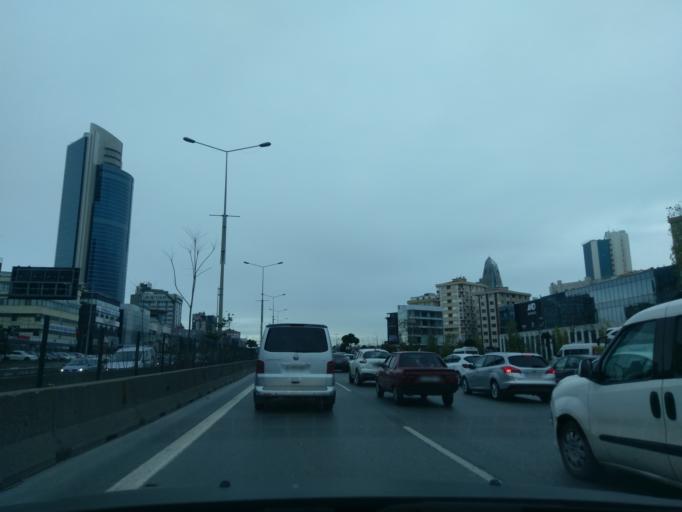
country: TR
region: Istanbul
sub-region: Atasehir
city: Atasehir
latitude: 40.9720
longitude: 29.1009
